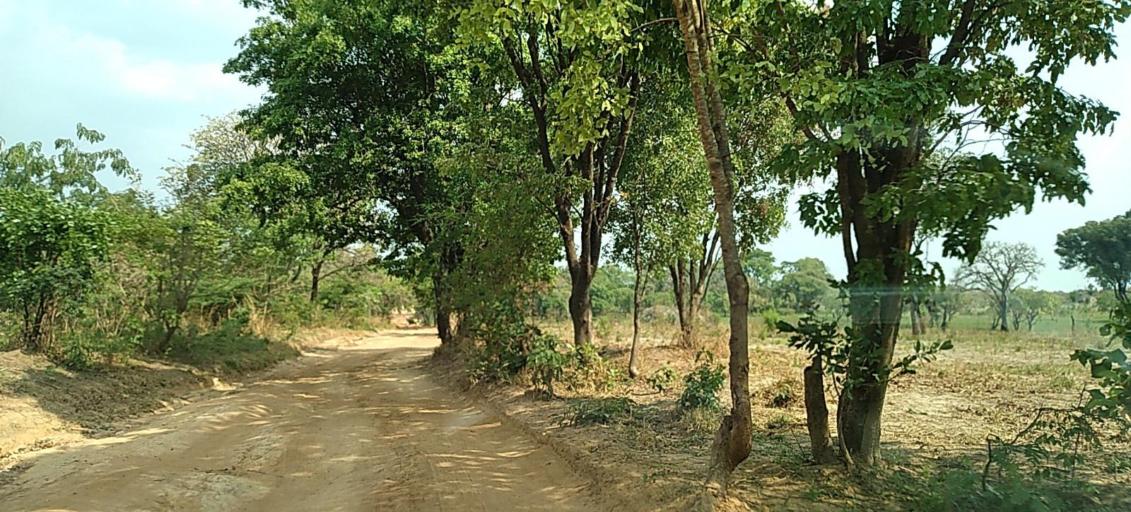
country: ZM
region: Copperbelt
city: Chingola
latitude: -12.7528
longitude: 27.7880
